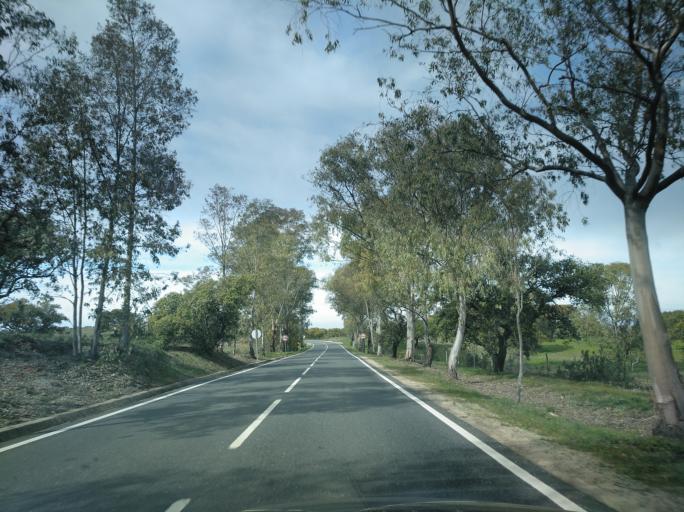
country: PT
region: Beja
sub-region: Mertola
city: Mertola
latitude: 37.7172
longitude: -7.7567
